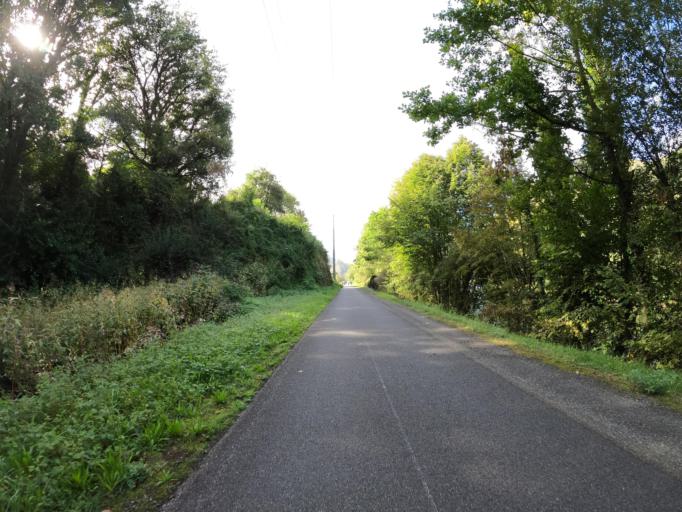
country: FR
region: Midi-Pyrenees
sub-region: Departement des Hautes-Pyrenees
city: Lourdes
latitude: 43.0591
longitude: -0.0415
